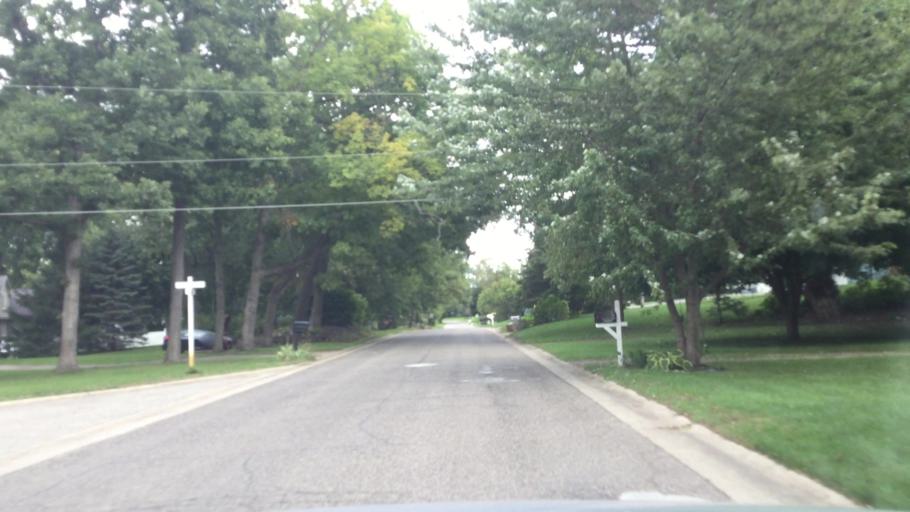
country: US
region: Michigan
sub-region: Livingston County
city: Brighton
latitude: 42.5567
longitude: -83.7516
